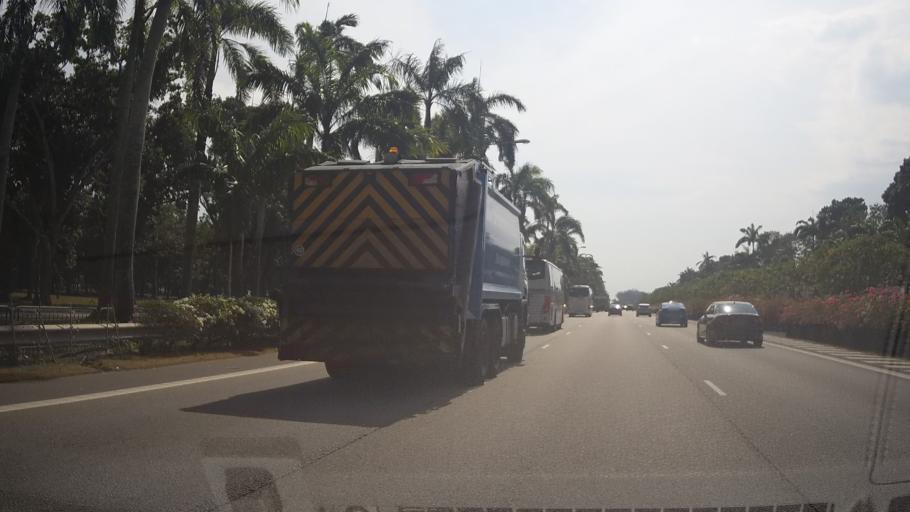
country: SG
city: Singapore
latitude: 1.3157
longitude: 103.9602
